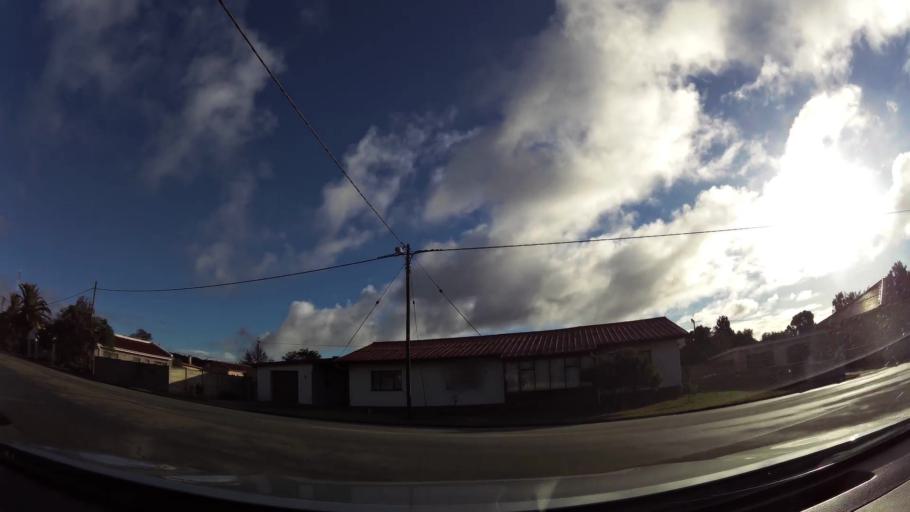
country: ZA
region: Western Cape
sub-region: Eden District Municipality
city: Riversdale
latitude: -34.2084
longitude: 21.5864
